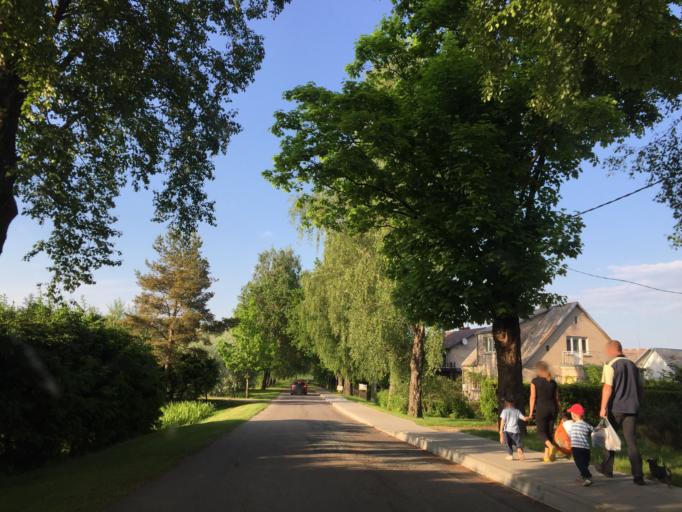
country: LT
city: Plateliai
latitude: 56.0433
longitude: 21.8218
